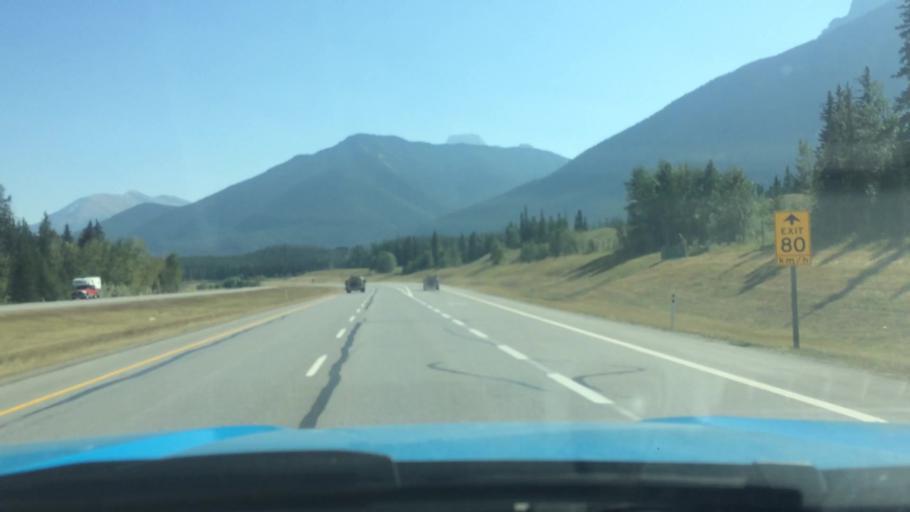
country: CA
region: Alberta
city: Canmore
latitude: 51.0614
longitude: -115.3219
